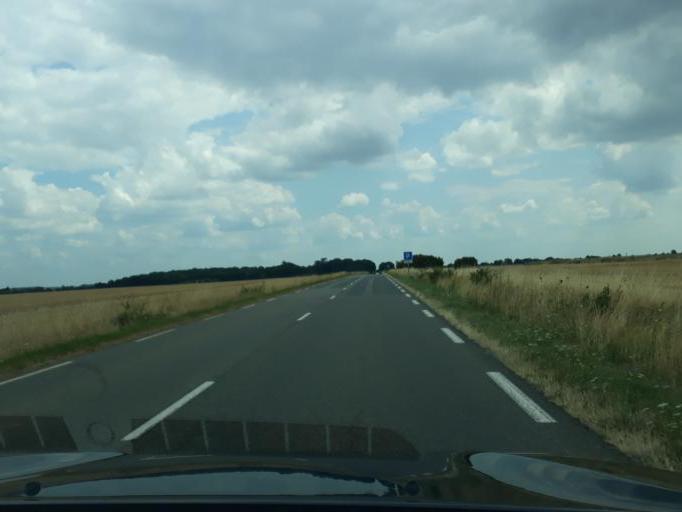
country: FR
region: Centre
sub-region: Departement du Cher
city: Avord
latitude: 47.0263
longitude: 2.6672
